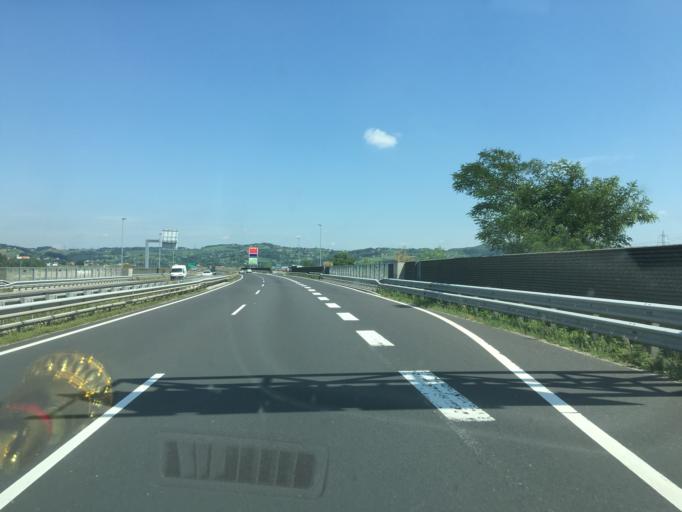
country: SI
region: Miklavz na Dravskem Polju
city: Miklavz na Dravskem Polju
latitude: 46.5278
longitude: 15.6982
